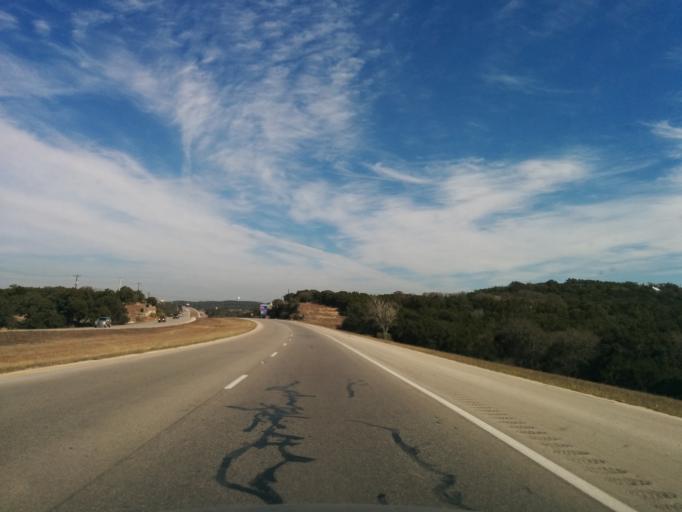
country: US
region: Texas
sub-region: Comal County
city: Bulverde
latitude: 29.7790
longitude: -98.4249
